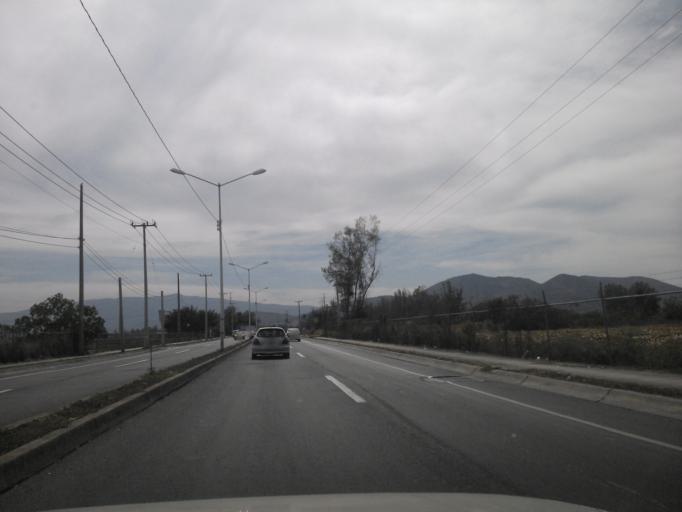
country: MX
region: Jalisco
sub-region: San Pedro Tlaquepaque
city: Paseo del Prado
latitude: 20.5473
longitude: -103.4011
